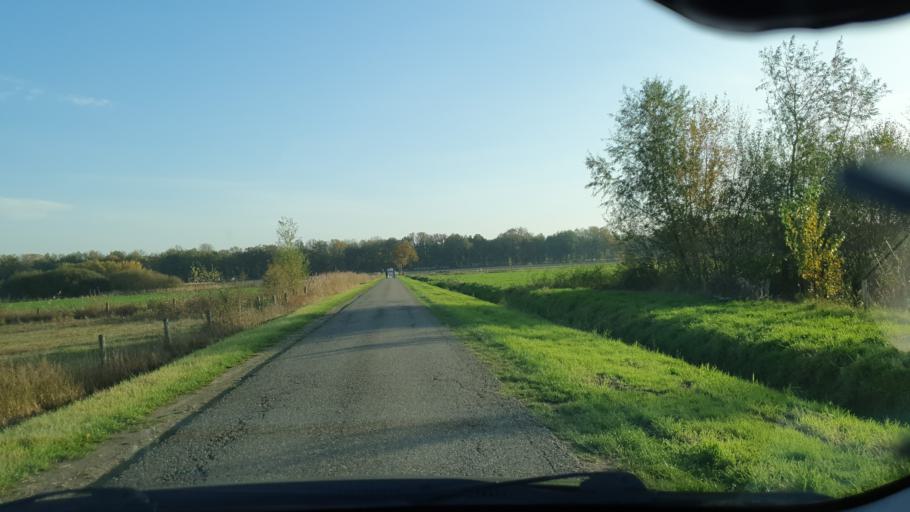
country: NL
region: Limburg
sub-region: Gemeente Roerdalen
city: Montfort
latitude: 51.1277
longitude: 5.9232
